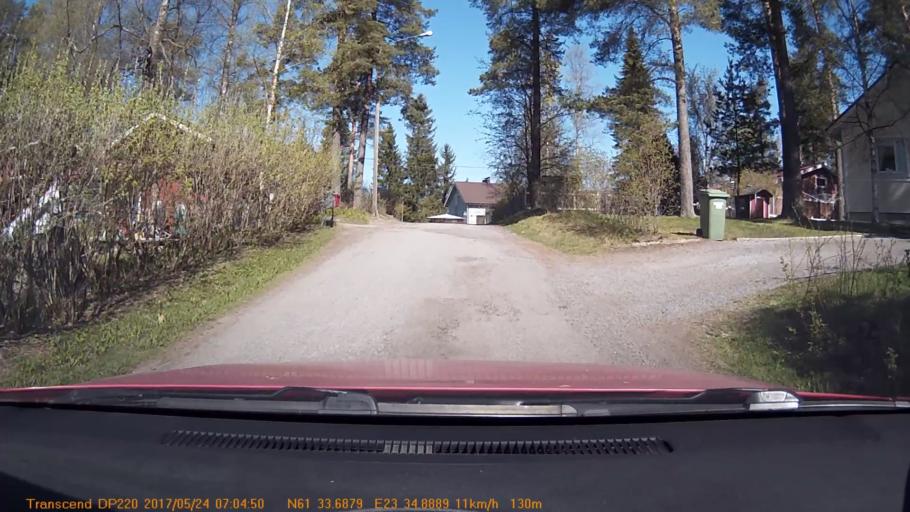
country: FI
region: Pirkanmaa
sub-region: Tampere
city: Yloejaervi
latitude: 61.5617
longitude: 23.5813
